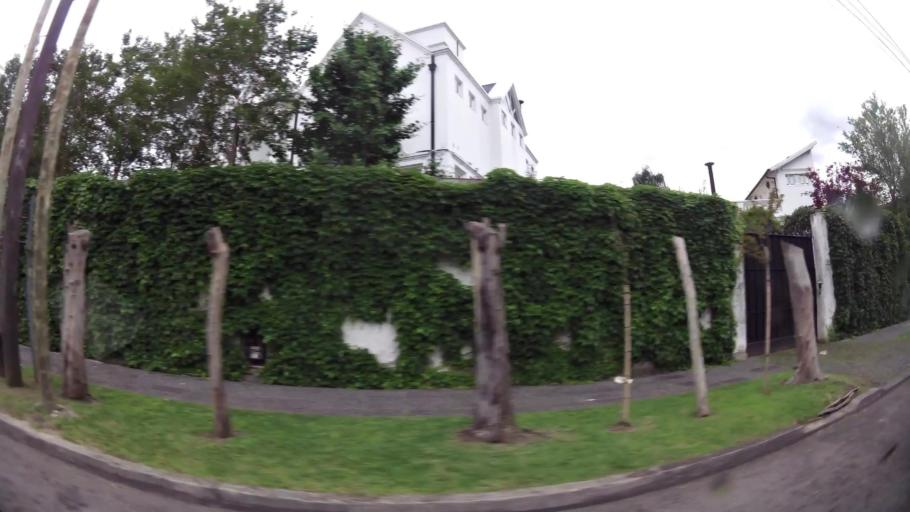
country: AR
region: Buenos Aires
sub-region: Partido de Lanus
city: Lanus
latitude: -34.6778
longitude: -58.4083
